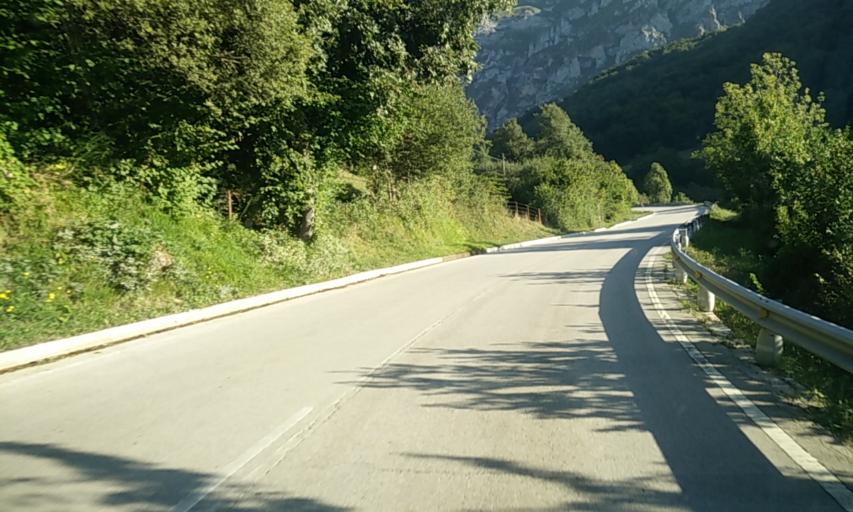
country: ES
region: Castille and Leon
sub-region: Provincia de Leon
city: Posada de Valdeon
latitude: 43.1381
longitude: -4.8108
